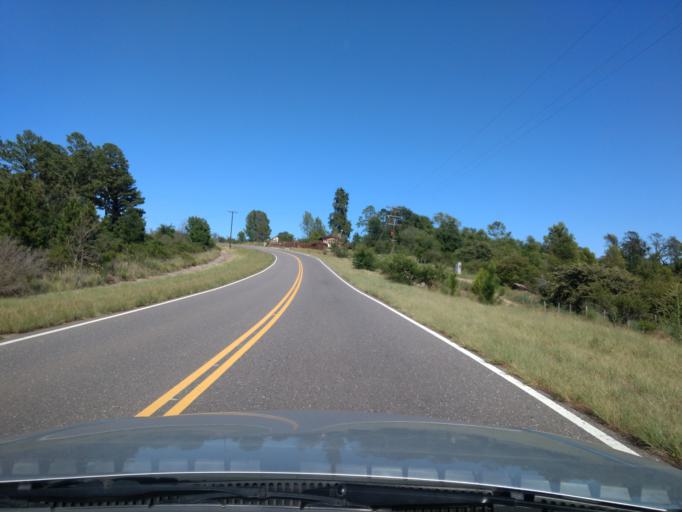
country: AR
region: Cordoba
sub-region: Departamento de Calamuchita
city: Villa General Belgrano
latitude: -31.9631
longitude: -64.6496
